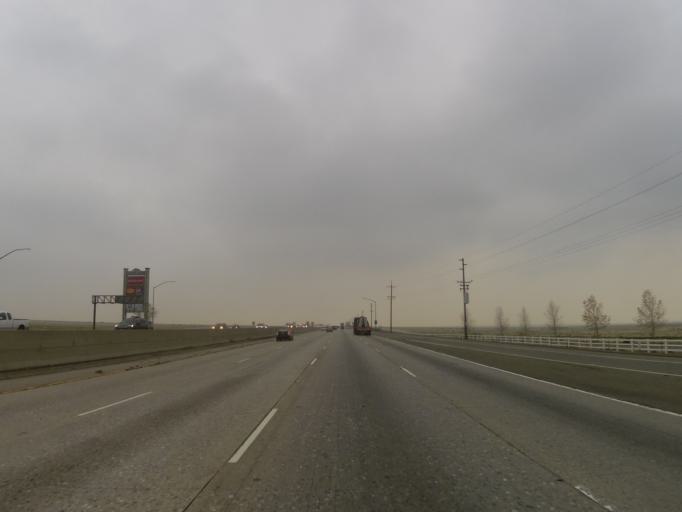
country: US
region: California
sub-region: Kern County
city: Frazier Park
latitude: 34.9435
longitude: -118.9316
